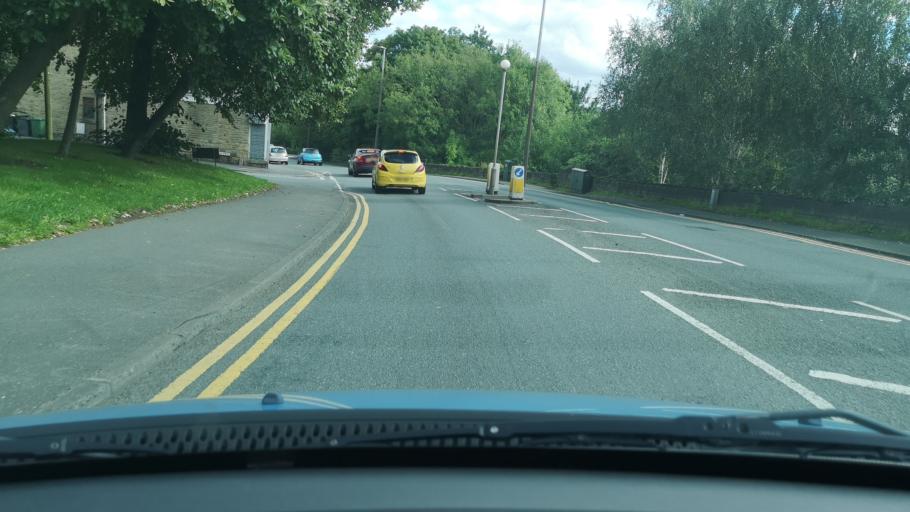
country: GB
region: England
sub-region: Kirklees
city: Liversedge
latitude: 53.7075
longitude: -1.6904
